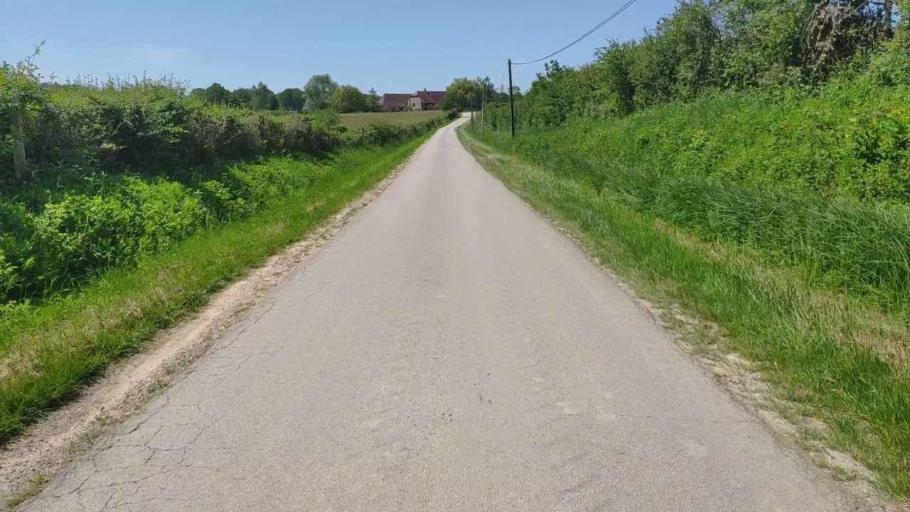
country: FR
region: Franche-Comte
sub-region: Departement du Jura
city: Bletterans
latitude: 46.7727
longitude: 5.4037
